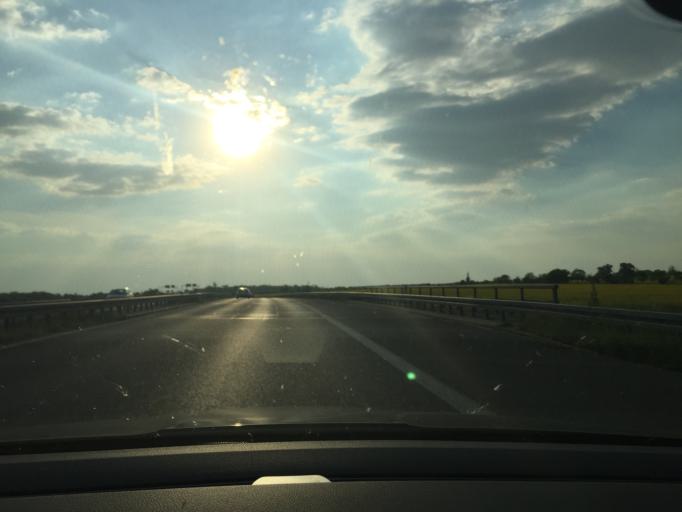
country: DE
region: Berlin
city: Lichtenrade
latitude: 52.3665
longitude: 13.4352
